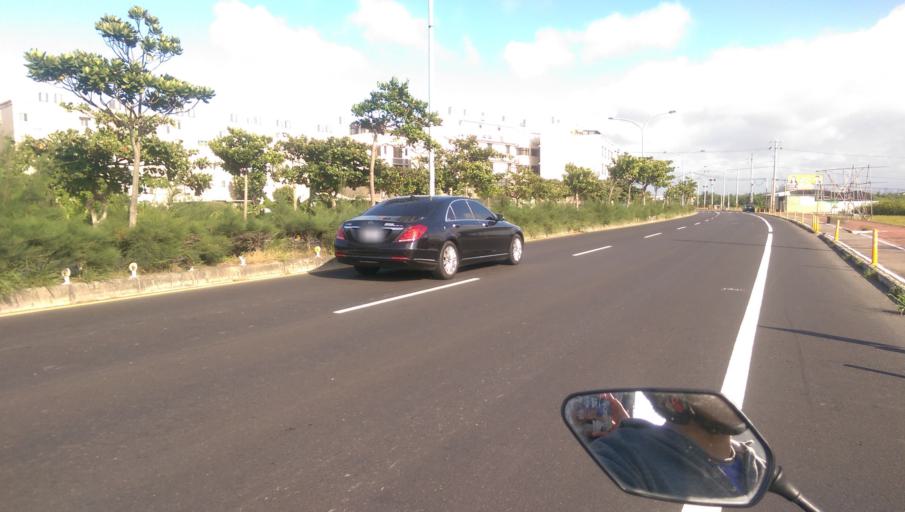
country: TW
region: Taiwan
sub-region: Hsinchu
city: Hsinchu
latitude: 24.8344
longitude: 120.9431
